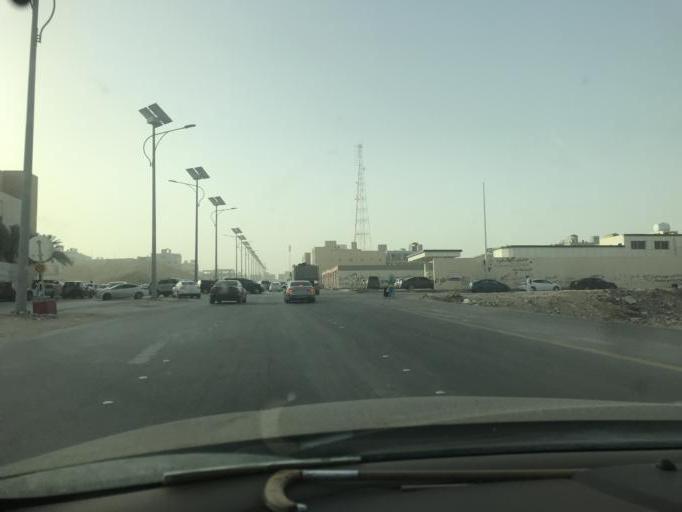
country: SA
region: Ar Riyad
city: Riyadh
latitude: 24.8429
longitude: 46.6656
